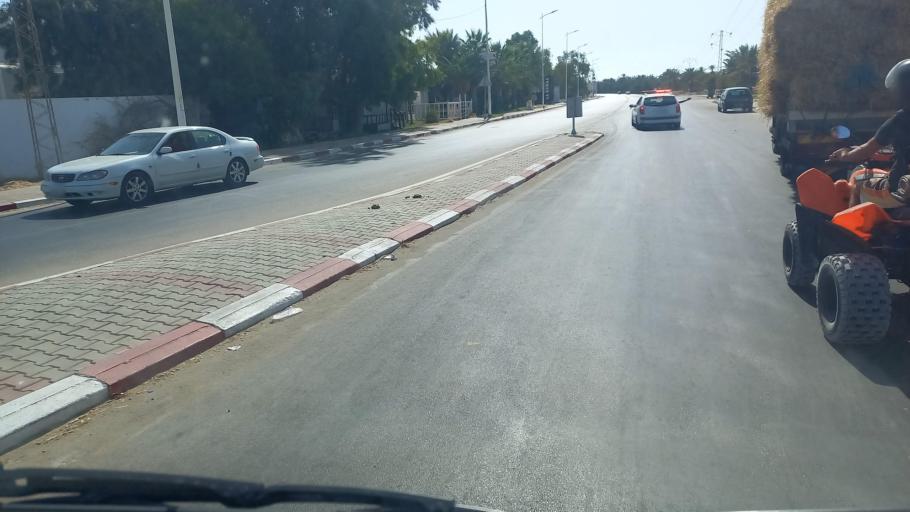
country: TN
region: Madanin
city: Midoun
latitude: 33.8388
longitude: 10.9932
